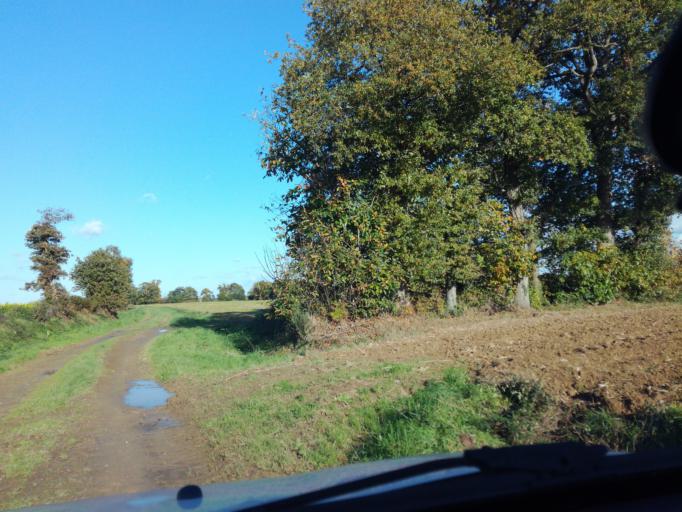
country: FR
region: Brittany
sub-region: Departement d'Ille-et-Vilaine
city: Chavagne
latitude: 48.0300
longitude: -1.7924
